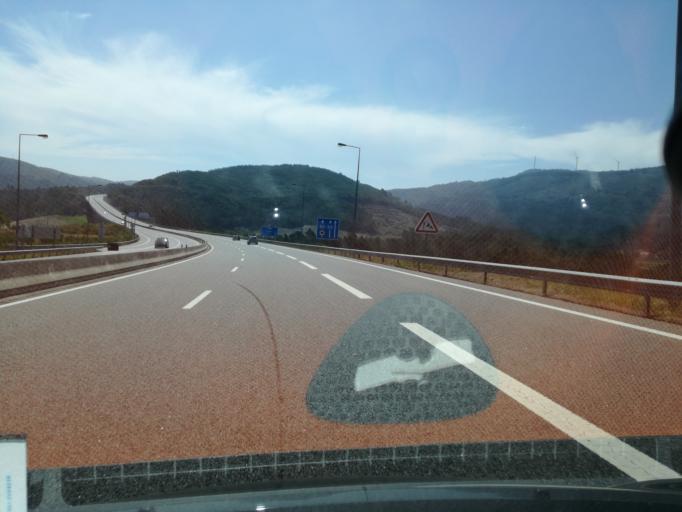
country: PT
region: Viana do Castelo
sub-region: Caminha
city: Vila Praia de Ancora
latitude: 41.8036
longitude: -8.8023
